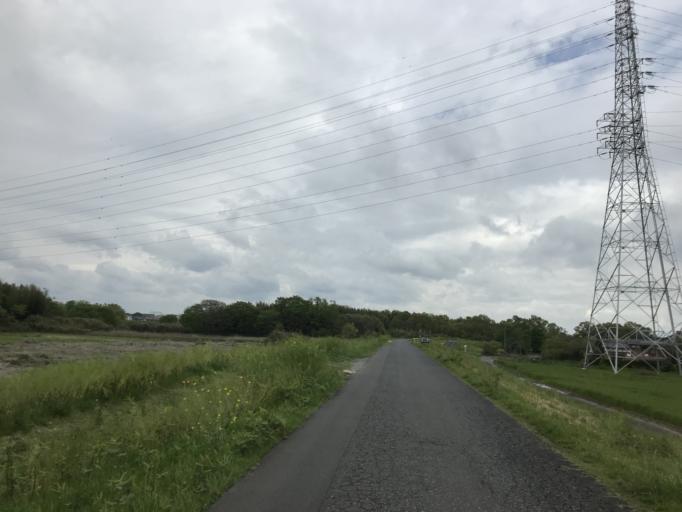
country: JP
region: Ibaraki
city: Mitsukaido
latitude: 36.0094
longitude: 139.9955
